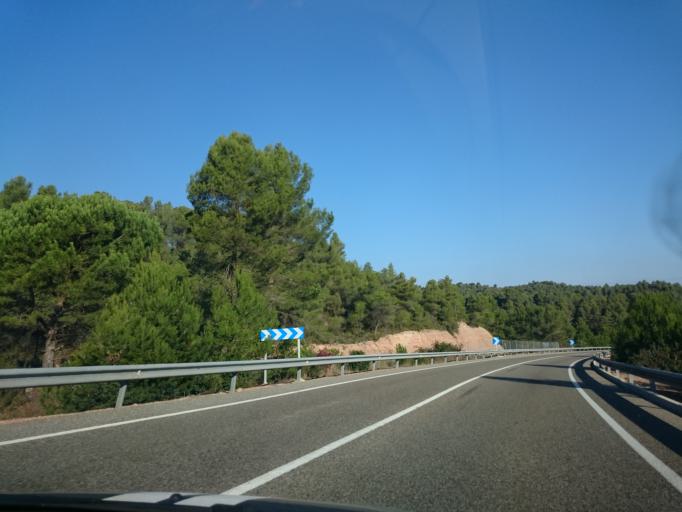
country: ES
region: Catalonia
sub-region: Provincia de Barcelona
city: Castellfollit del Boix
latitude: 41.6377
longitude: 1.6955
